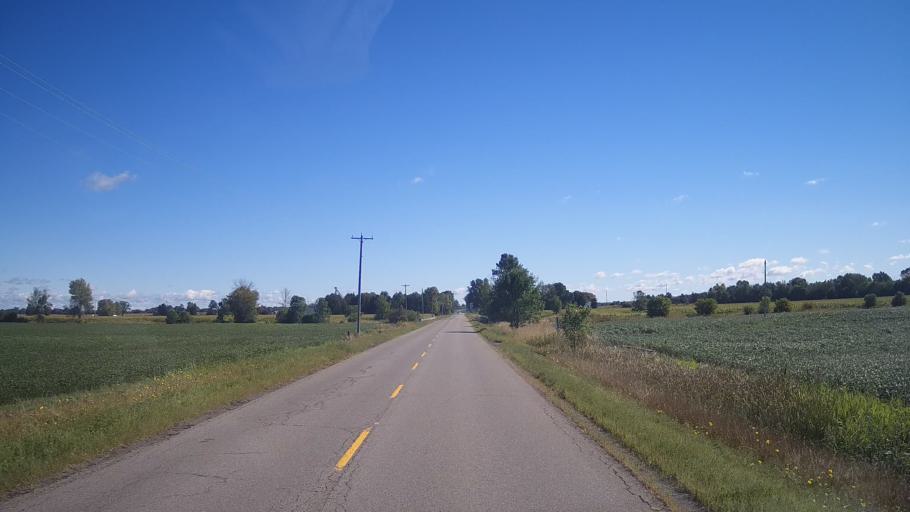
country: CA
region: Ontario
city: Prescott
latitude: 44.9204
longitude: -75.3552
